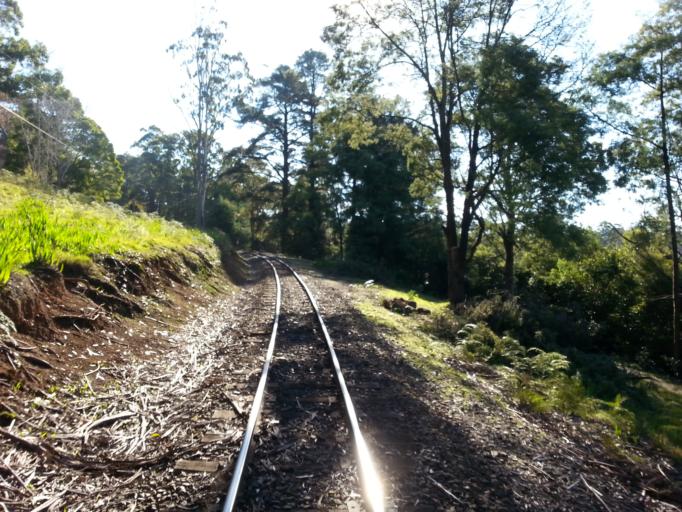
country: AU
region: Victoria
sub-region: Cardinia
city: Emerald
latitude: -37.9333
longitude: 145.4522
